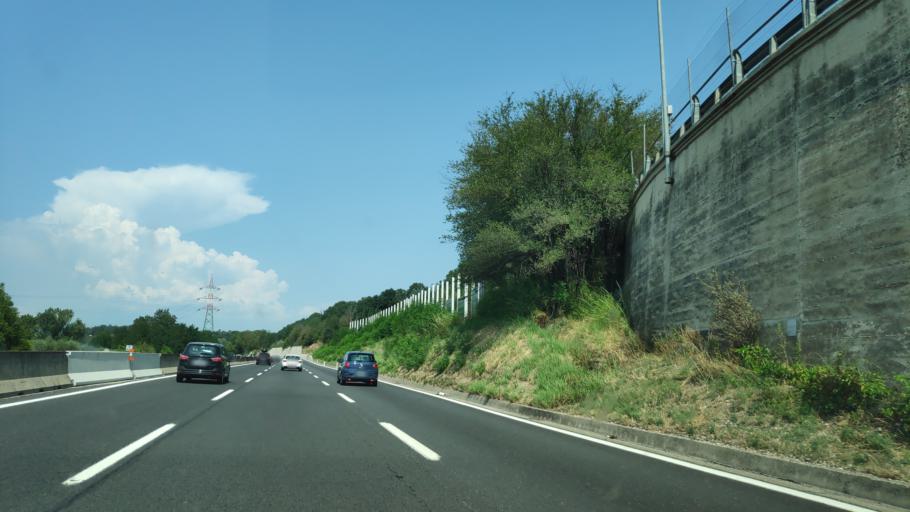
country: IT
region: Latium
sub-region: Provincia di Rieti
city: Magliano Sabina
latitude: 42.3846
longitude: 12.4708
